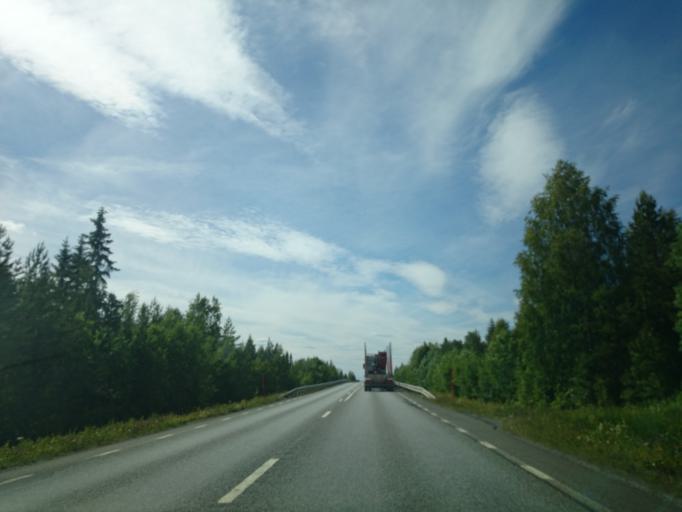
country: SE
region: Jaemtland
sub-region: Krokoms Kommun
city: Krokom
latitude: 63.3221
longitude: 14.2122
